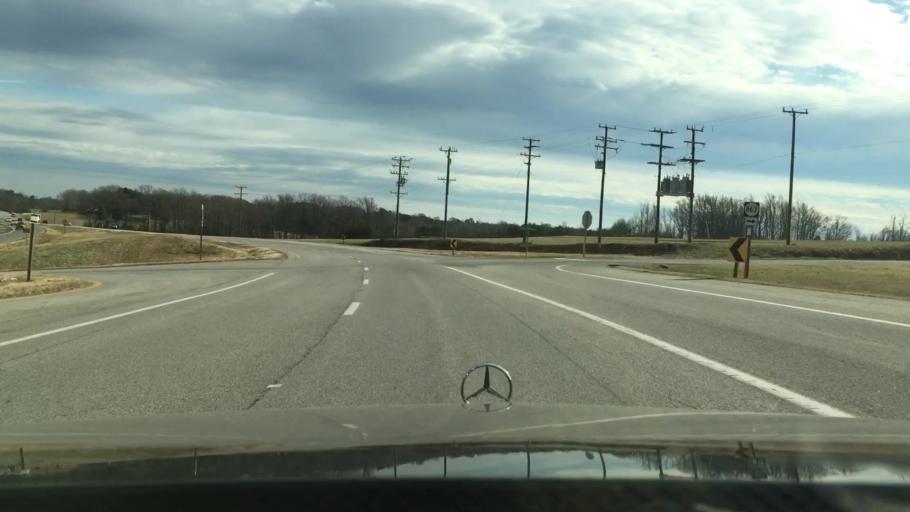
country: US
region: Virginia
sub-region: Pittsylvania County
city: Mount Hermon
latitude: 36.7224
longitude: -79.3852
